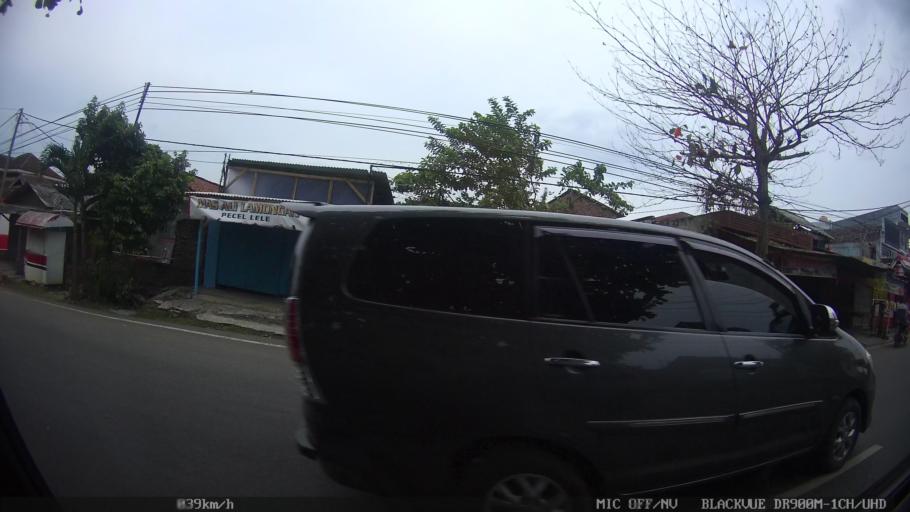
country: ID
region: Lampung
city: Kedaton
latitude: -5.4023
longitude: 105.2433
